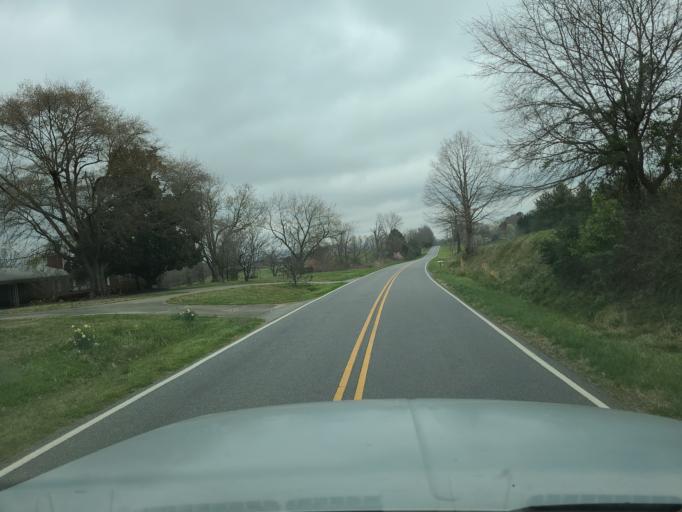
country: US
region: North Carolina
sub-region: Cleveland County
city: Shelby
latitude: 35.4232
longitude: -81.6443
